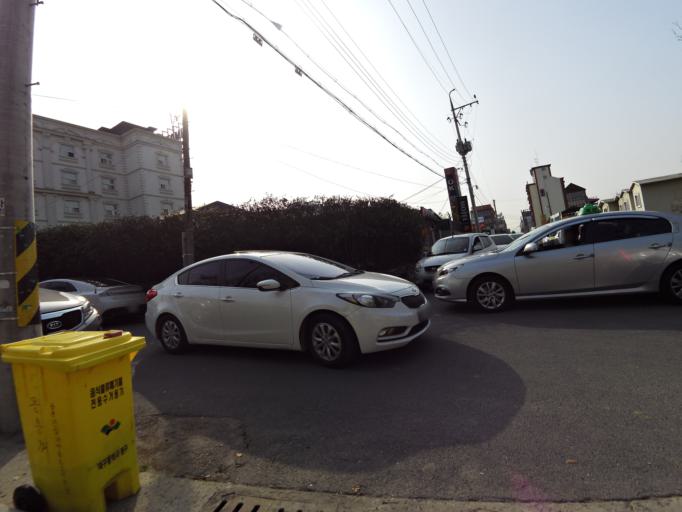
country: KR
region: Daegu
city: Daegu
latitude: 35.8788
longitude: 128.6556
